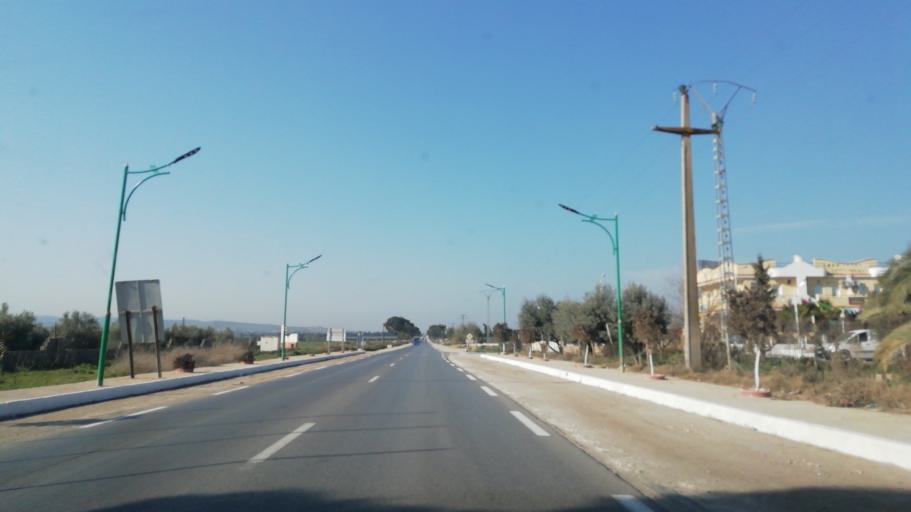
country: DZ
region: Relizane
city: Relizane
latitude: 35.7329
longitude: 0.4515
